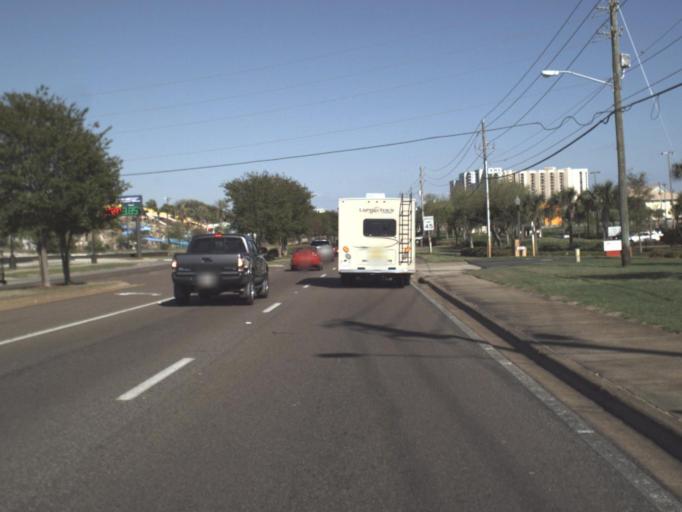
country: US
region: Florida
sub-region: Okaloosa County
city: Destin
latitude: 30.3880
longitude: -86.4767
